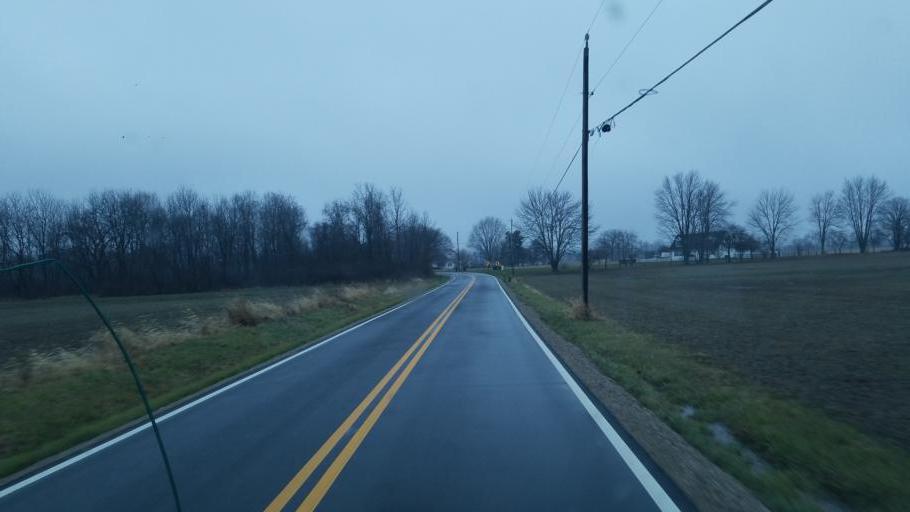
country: US
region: Ohio
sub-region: Delaware County
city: Delaware
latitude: 40.2711
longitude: -83.0041
